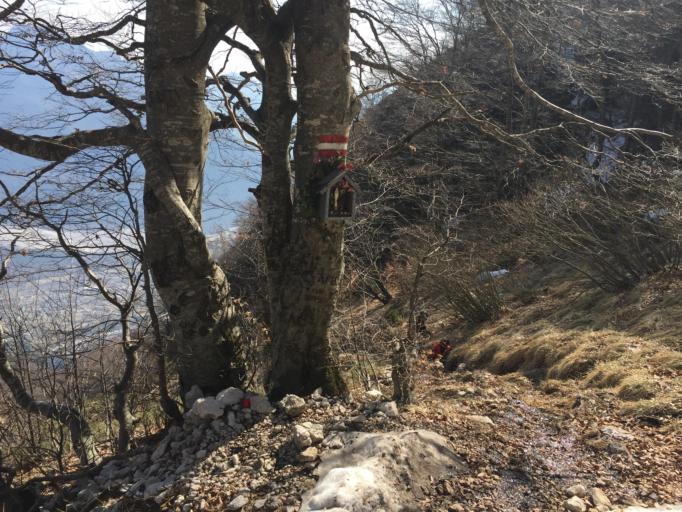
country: IT
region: Friuli Venezia Giulia
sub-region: Provincia di Udine
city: Amaro
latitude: 46.3967
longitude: 13.0792
